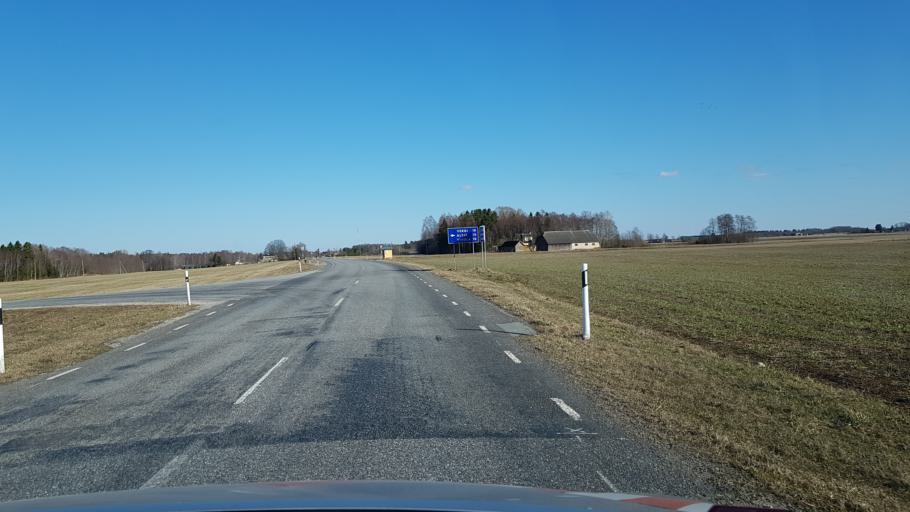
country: EE
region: Laeaene-Virumaa
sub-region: Haljala vald
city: Haljala
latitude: 59.4628
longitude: 26.1950
